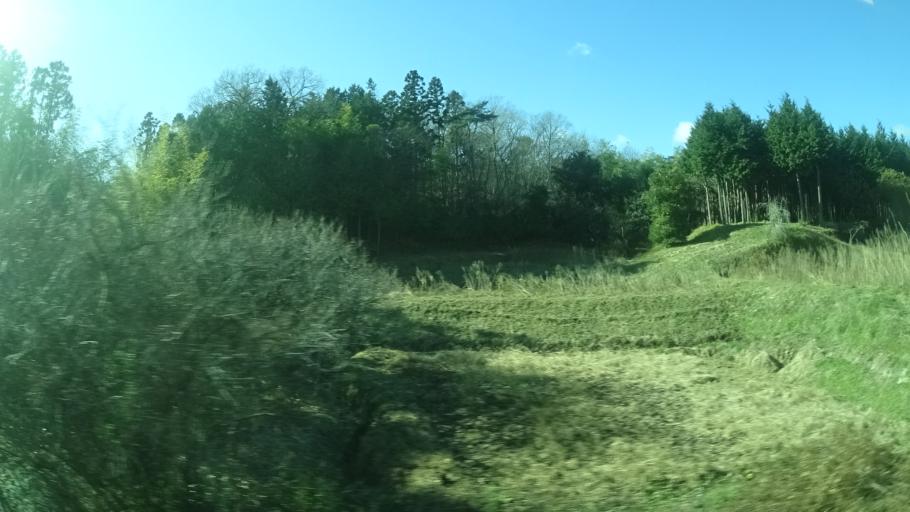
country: JP
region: Fukushima
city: Namie
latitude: 37.7278
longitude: 140.9515
